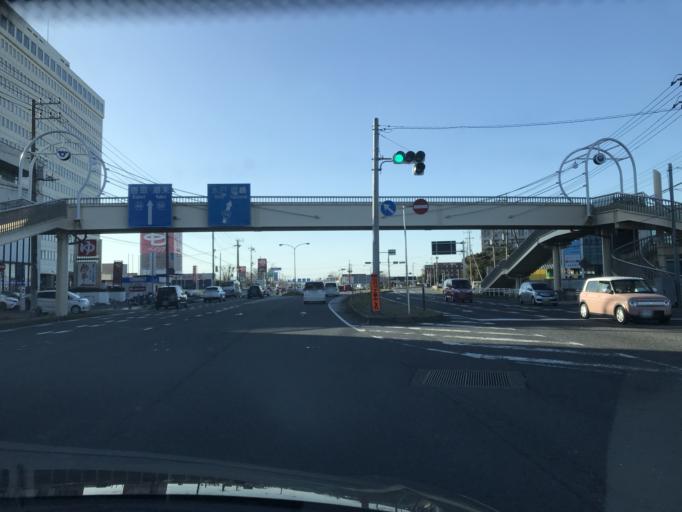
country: JP
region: Chiba
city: Omigawa
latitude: 35.8998
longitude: 140.6390
